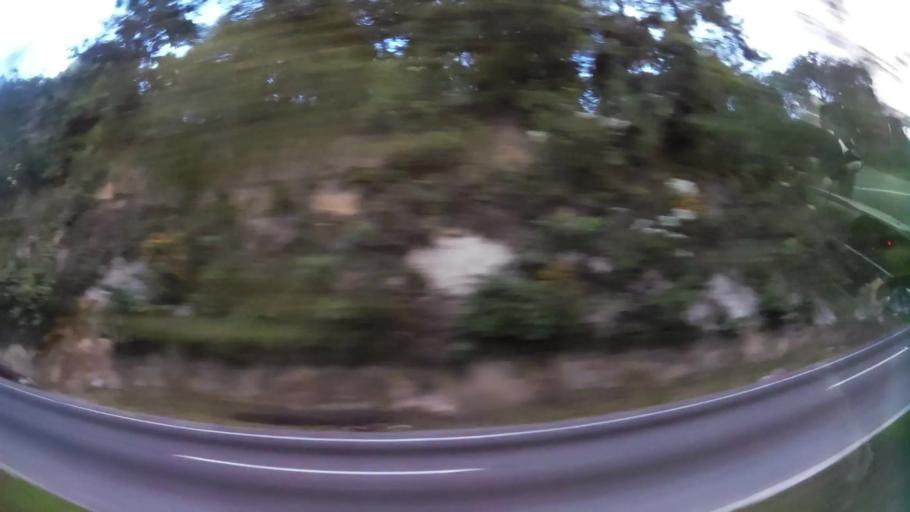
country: GT
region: Sacatepequez
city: San Lucas Sacatepequez
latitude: 14.6050
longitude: -90.6501
